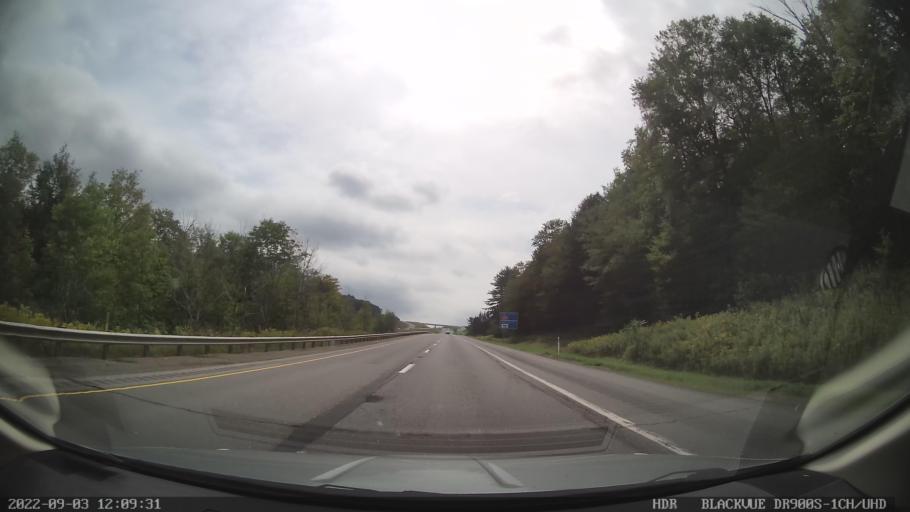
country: US
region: Pennsylvania
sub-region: Tioga County
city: Blossburg
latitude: 41.4661
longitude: -77.1365
